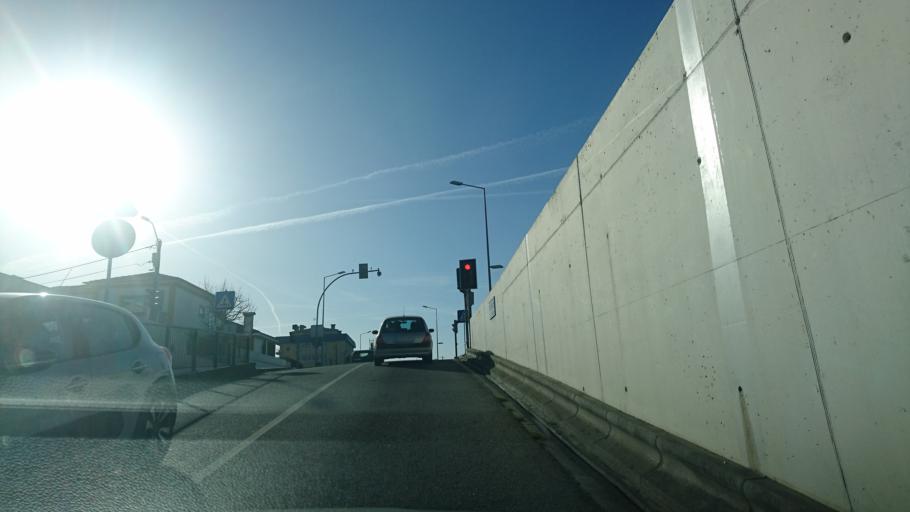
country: PT
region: Aveiro
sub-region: Ovar
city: Esmoriz
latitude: 40.9550
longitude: -8.6358
